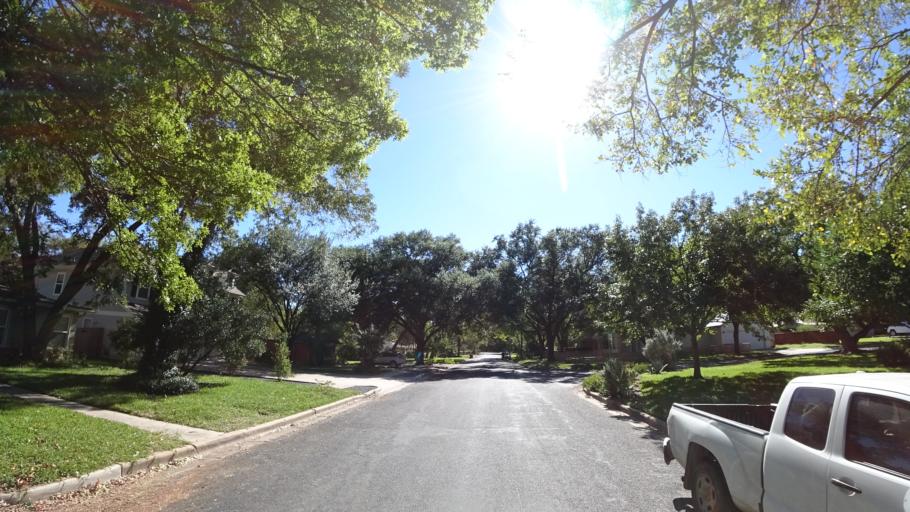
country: US
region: Texas
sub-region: Travis County
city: West Lake Hills
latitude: 30.3230
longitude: -97.7533
